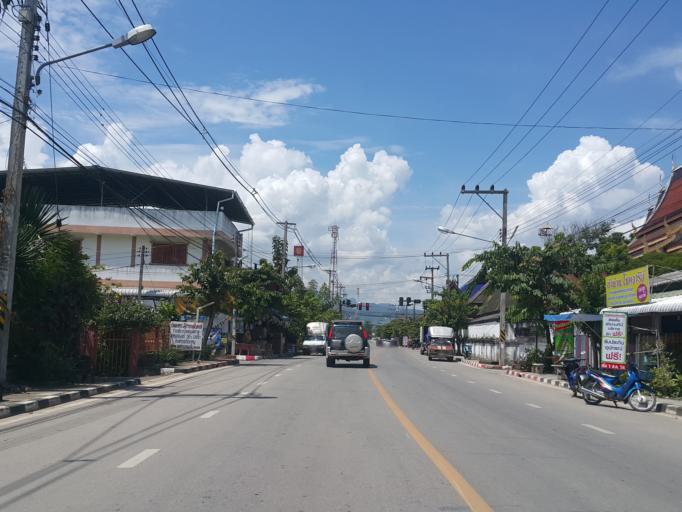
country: TH
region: Chiang Mai
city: Phrao
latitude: 19.3684
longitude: 99.2055
